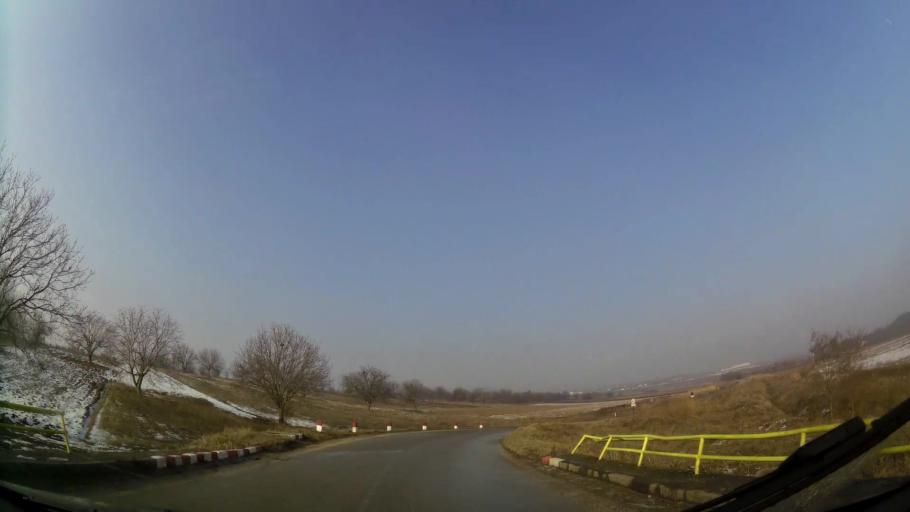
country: MK
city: Kadino
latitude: 41.9733
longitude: 21.6072
